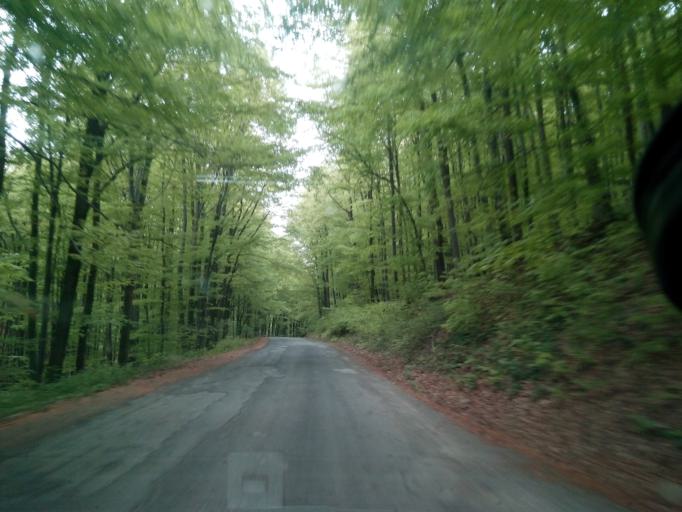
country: SK
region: Kosicky
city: Secovce
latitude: 48.8127
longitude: 21.5157
